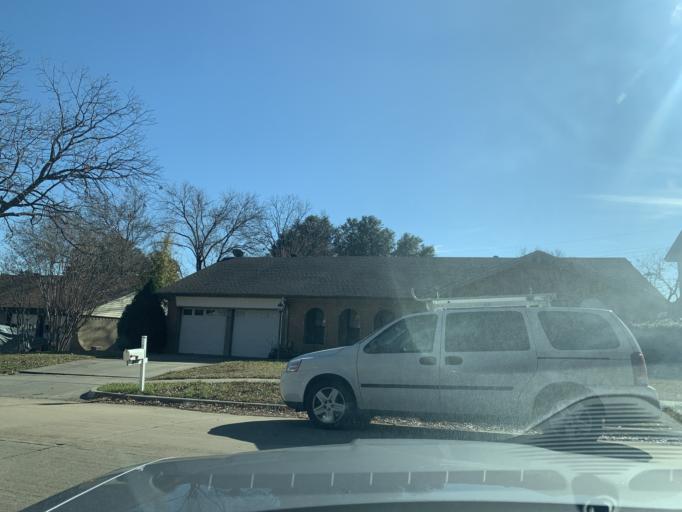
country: US
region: Texas
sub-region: Tarrant County
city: Bedford
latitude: 32.8418
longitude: -97.1555
